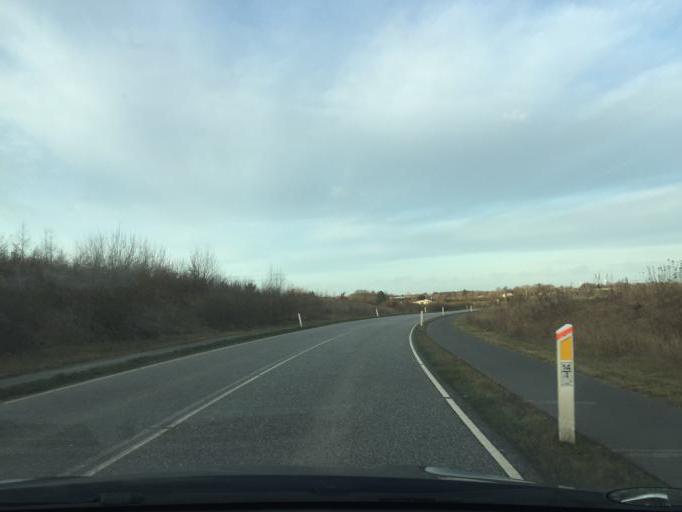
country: DK
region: South Denmark
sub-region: Faaborg-Midtfyn Kommune
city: Arslev
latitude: 55.2863
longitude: 10.4495
